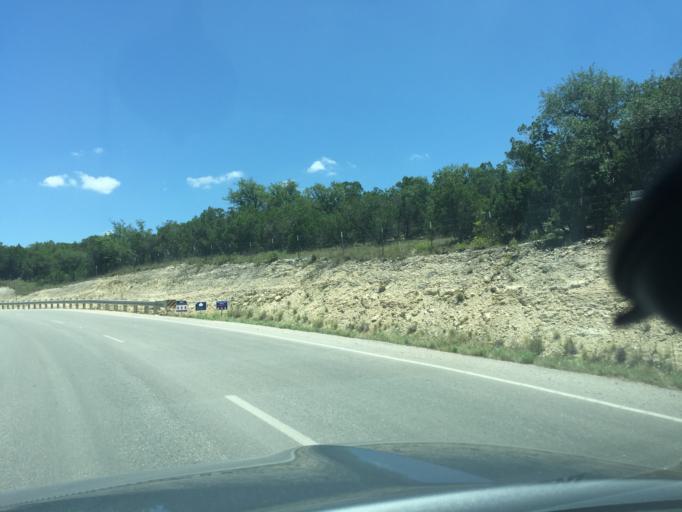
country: US
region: Texas
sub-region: Bexar County
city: Timberwood Park
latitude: 29.7126
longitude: -98.4651
